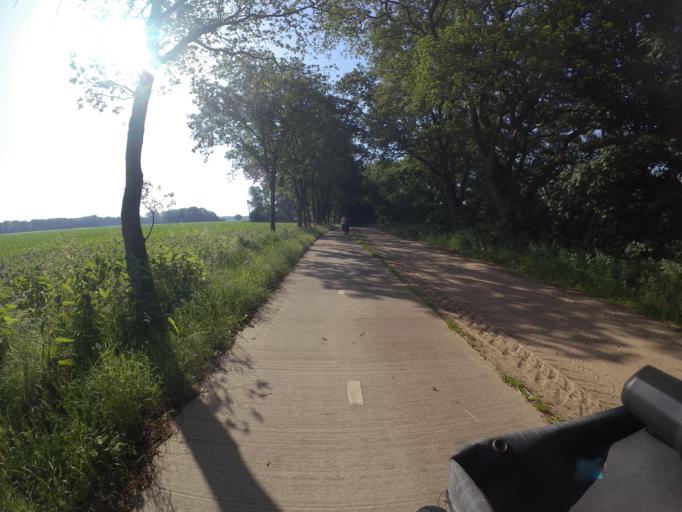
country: NL
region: Overijssel
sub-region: Gemeente Dalfsen
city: Dalfsen
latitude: 52.5253
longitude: 6.3066
